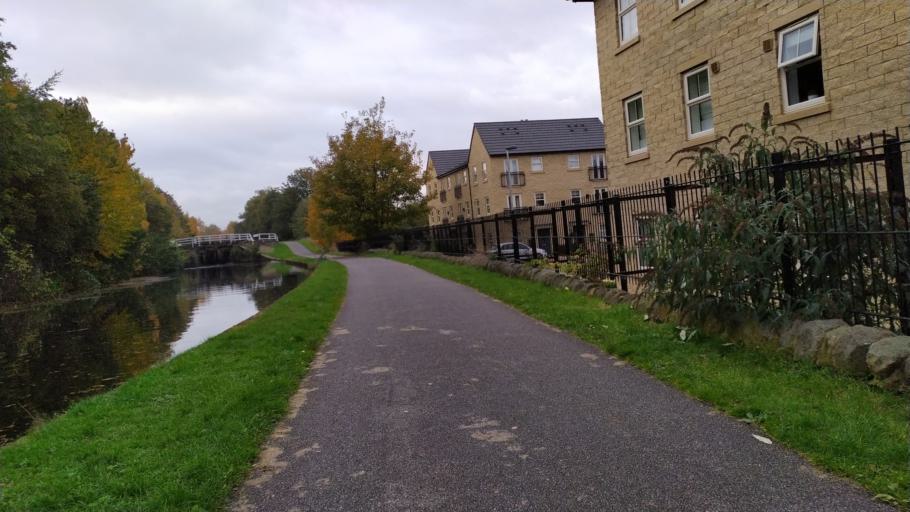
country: GB
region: England
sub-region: City and Borough of Leeds
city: Leeds
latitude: 53.7987
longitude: -1.5688
